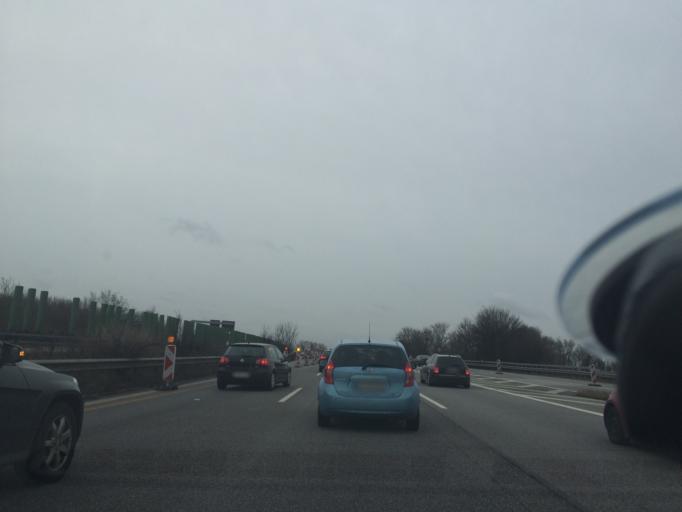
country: DE
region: Hamburg
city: Harburg
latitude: 53.4804
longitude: 10.0230
